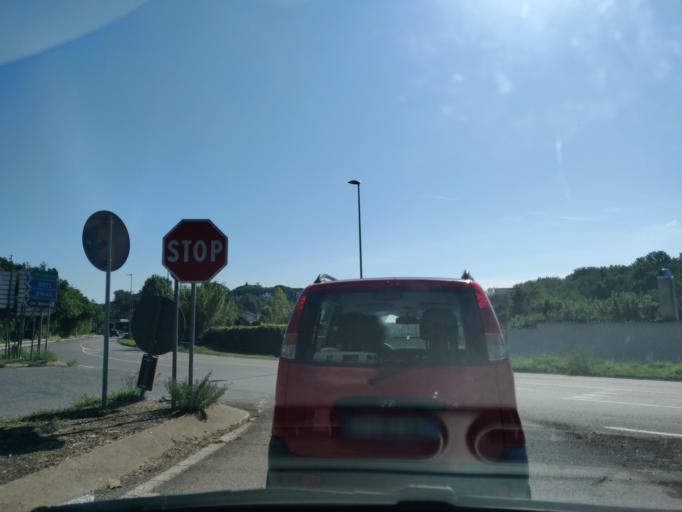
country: IT
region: Latium
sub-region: Provincia di Viterbo
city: Viterbo
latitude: 42.4186
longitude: 12.0802
